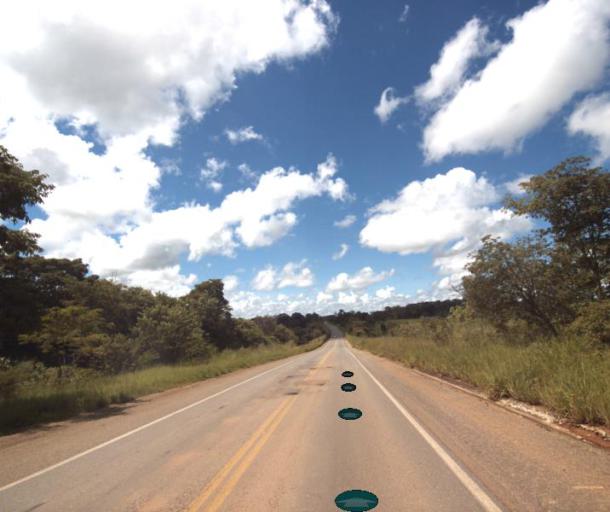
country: BR
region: Goias
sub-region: Petrolina De Goias
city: Petrolina de Goias
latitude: -16.0010
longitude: -49.1396
